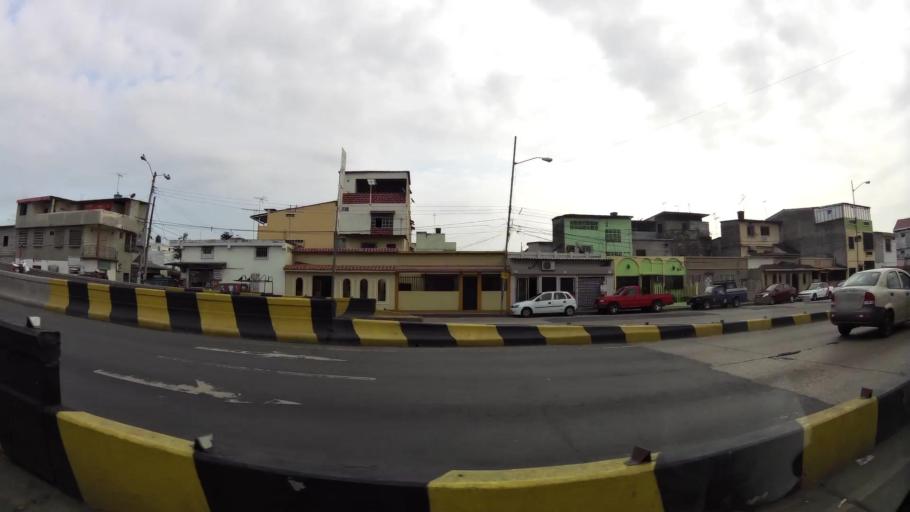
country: EC
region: Guayas
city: Guayaquil
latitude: -2.2391
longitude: -79.8948
